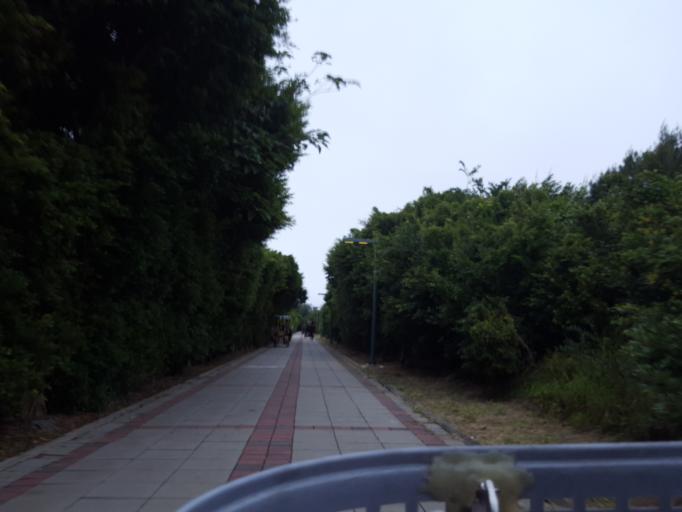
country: TW
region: Taiwan
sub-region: Hsinchu
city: Hsinchu
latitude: 24.8409
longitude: 120.9208
